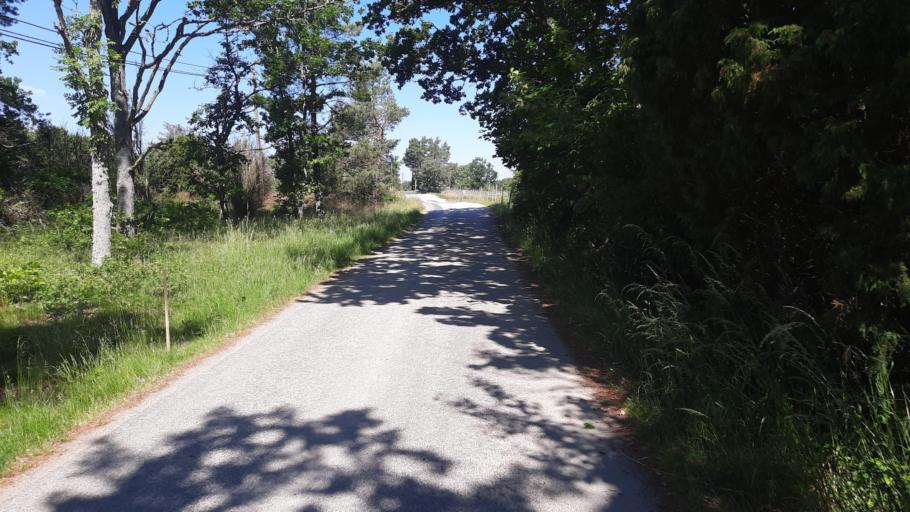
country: SE
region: Blekinge
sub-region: Karlskrona Kommun
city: Jaemjoe
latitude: 56.1491
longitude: 15.7693
